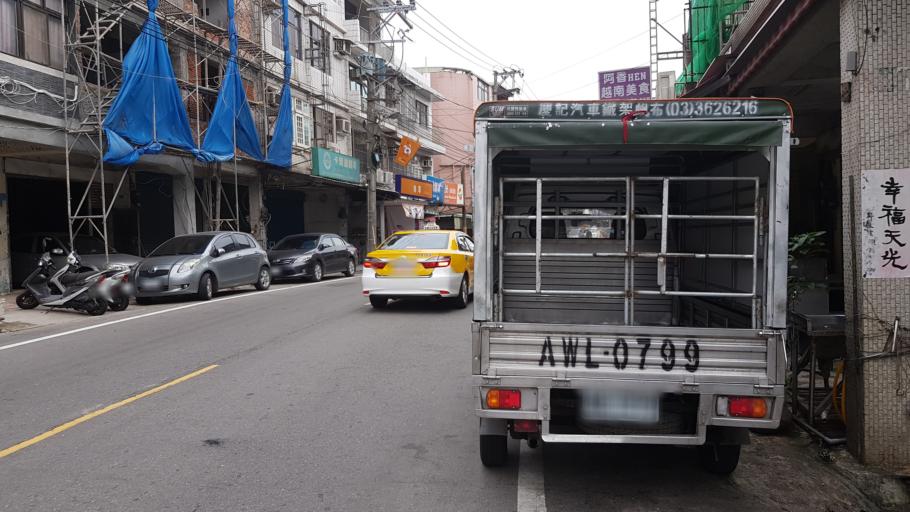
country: TW
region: Taiwan
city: Taoyuan City
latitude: 25.0785
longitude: 121.2575
